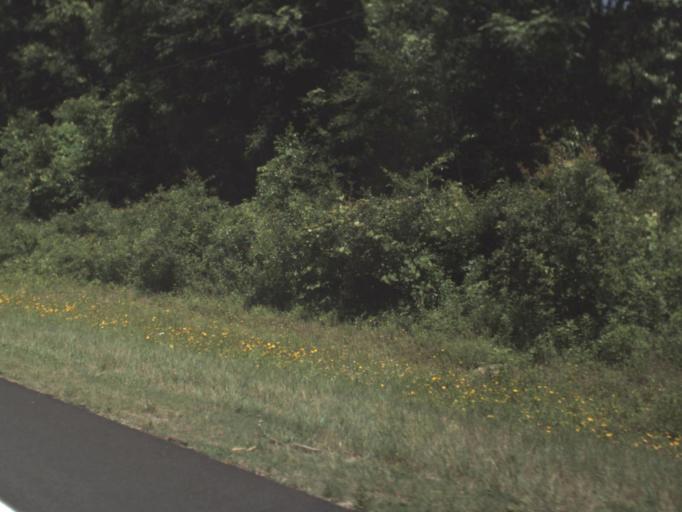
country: US
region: Florida
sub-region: Suwannee County
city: Wellborn
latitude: 30.2029
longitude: -82.7897
